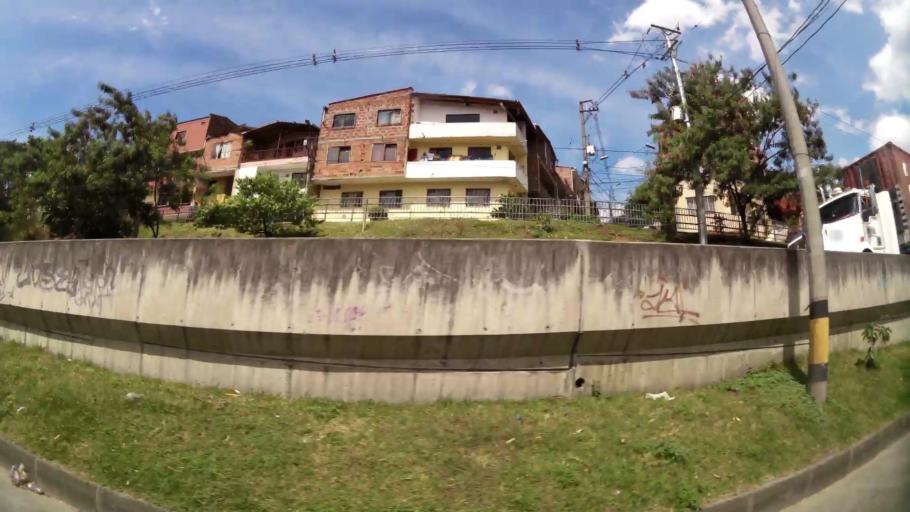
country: CO
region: Antioquia
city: Bello
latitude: 6.3044
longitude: -75.5579
